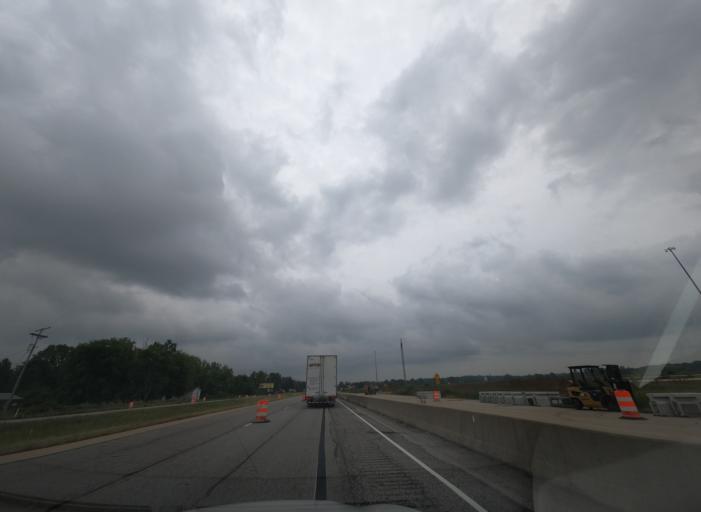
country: US
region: Indiana
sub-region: Vigo County
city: West Terre Haute
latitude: 39.4370
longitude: -87.5285
